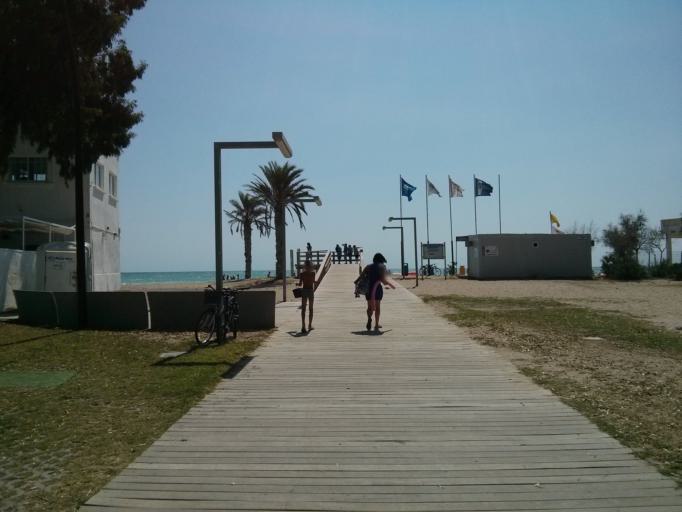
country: ES
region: Valencia
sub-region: Provincia de Castello
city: Moncofar
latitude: 39.8001
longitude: -0.1303
